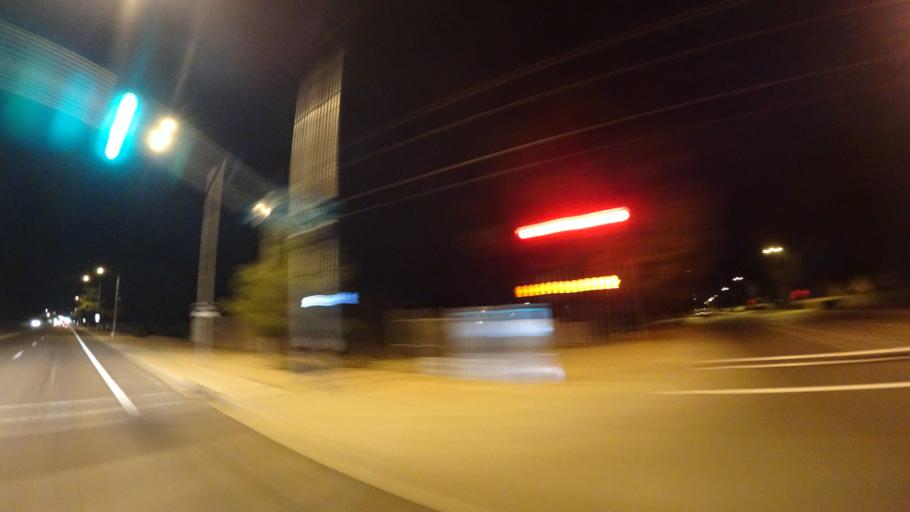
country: US
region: Arizona
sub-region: Maricopa County
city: Gilbert
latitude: 33.4010
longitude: -111.7537
